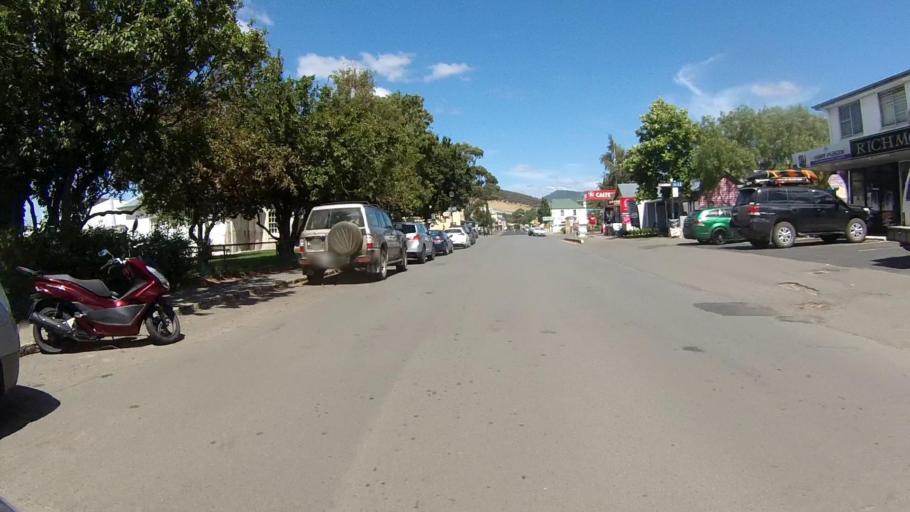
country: AU
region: Tasmania
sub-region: Clarence
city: Cambridge
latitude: -42.7350
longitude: 147.4384
